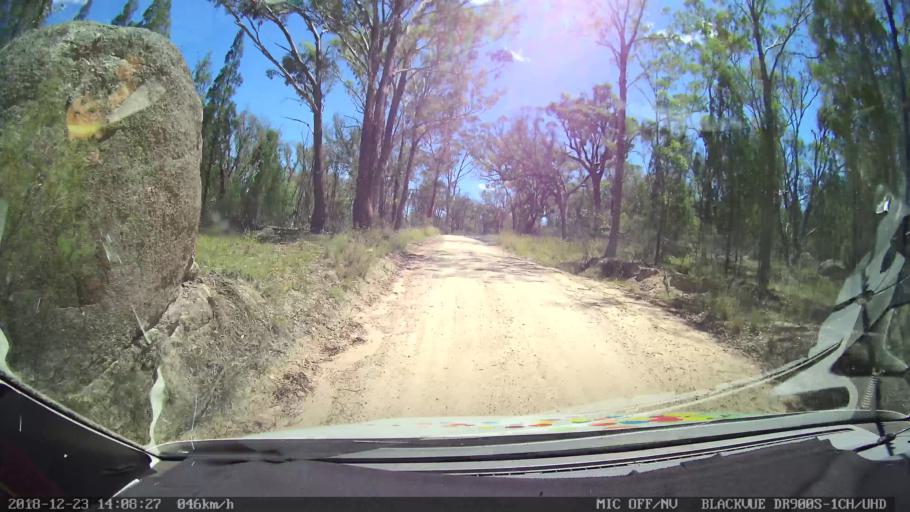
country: AU
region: New South Wales
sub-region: Tamworth Municipality
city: Manilla
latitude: -30.6421
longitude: 151.0678
